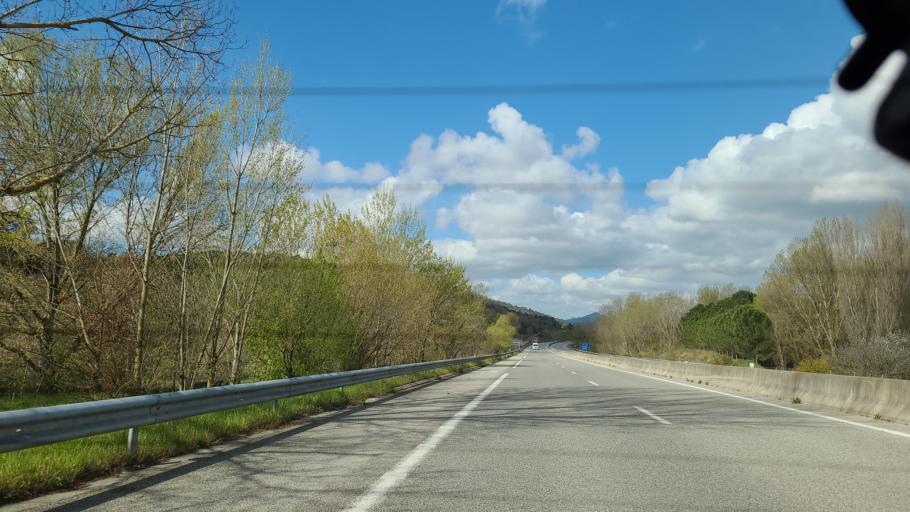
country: FR
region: Provence-Alpes-Cote d'Azur
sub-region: Departement du Var
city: Pignans
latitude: 43.2896
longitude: 6.2155
